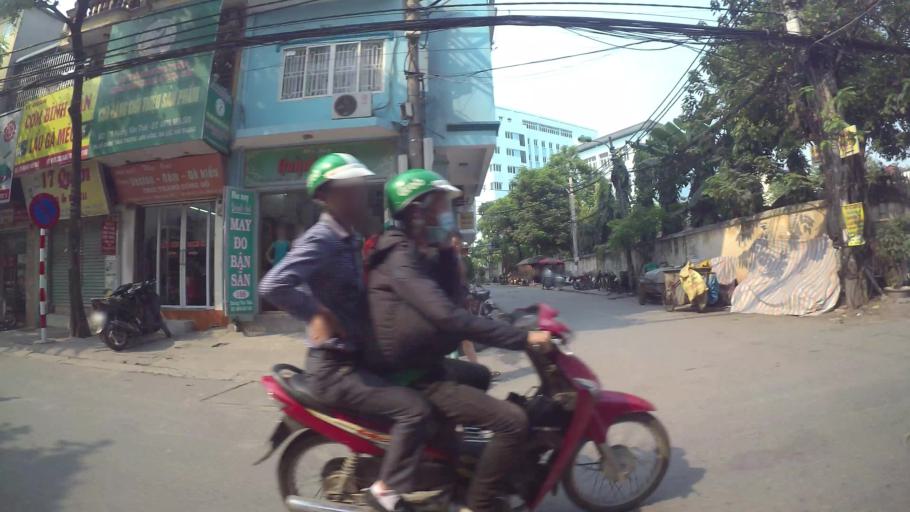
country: VN
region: Ha Noi
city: Dong Da
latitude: 20.9975
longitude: 105.8234
